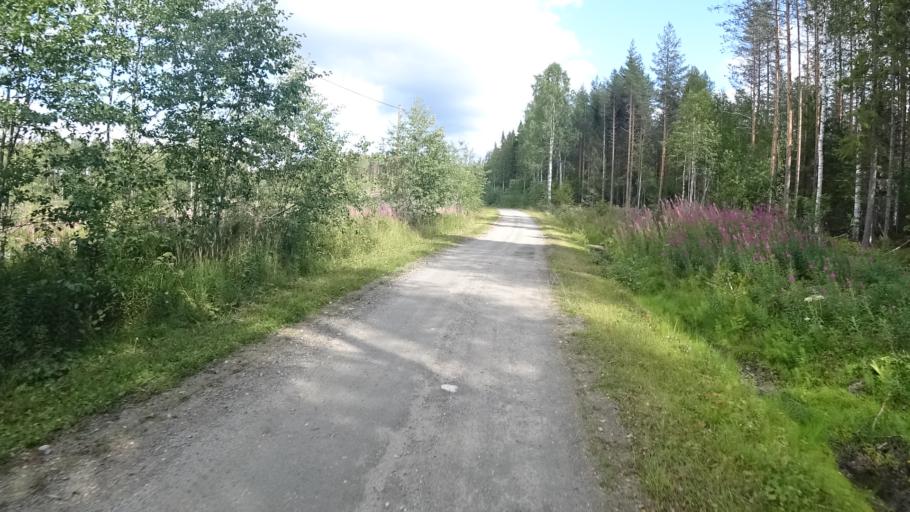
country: FI
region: North Karelia
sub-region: Joensuu
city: Ilomantsi
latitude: 62.6234
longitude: 31.2495
